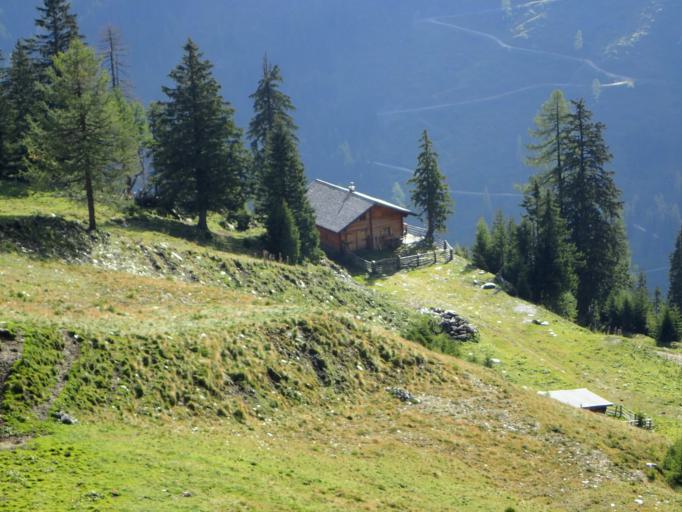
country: AT
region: Salzburg
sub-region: Politischer Bezirk Sankt Johann im Pongau
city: Huttschlag
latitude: 47.1413
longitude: 13.2256
